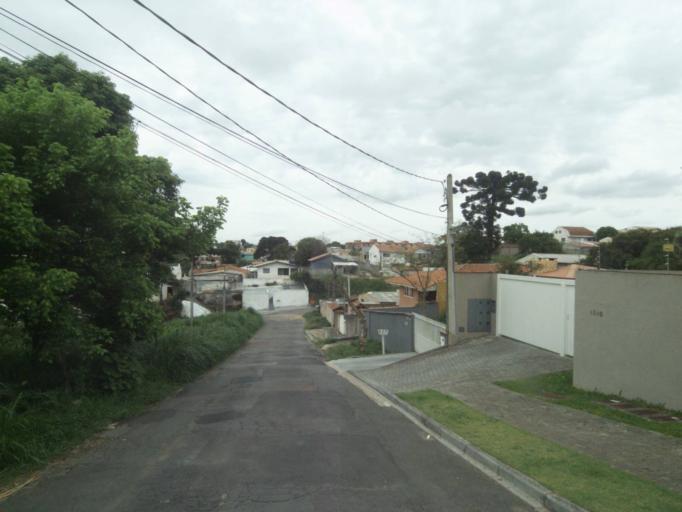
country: BR
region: Parana
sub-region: Curitiba
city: Curitiba
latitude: -25.3922
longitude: -49.2937
